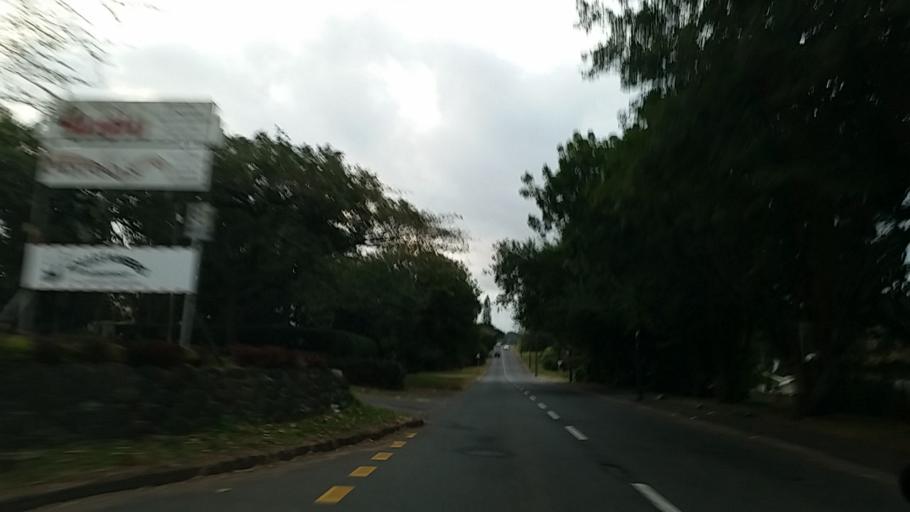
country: ZA
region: KwaZulu-Natal
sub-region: eThekwini Metropolitan Municipality
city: Berea
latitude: -29.8531
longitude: 30.9087
